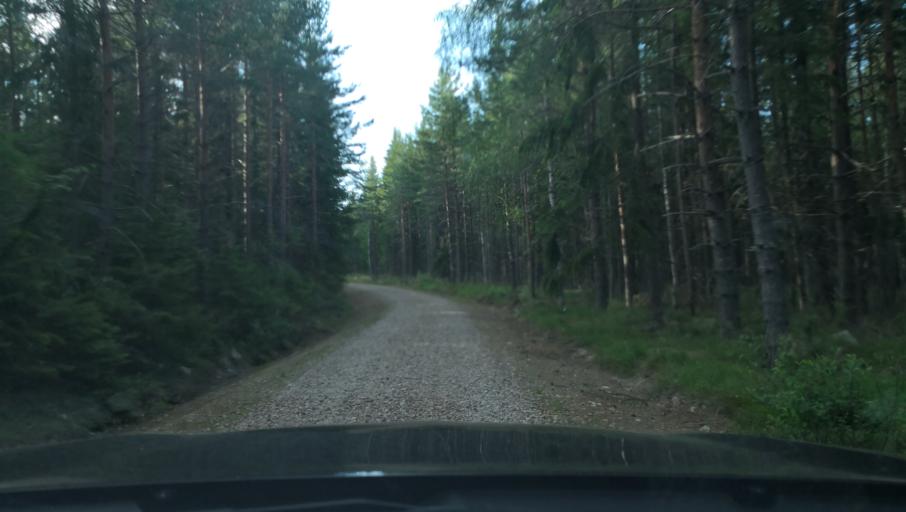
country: SE
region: Dalarna
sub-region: Ludvika Kommun
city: Ludvika
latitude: 60.0731
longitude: 15.2915
